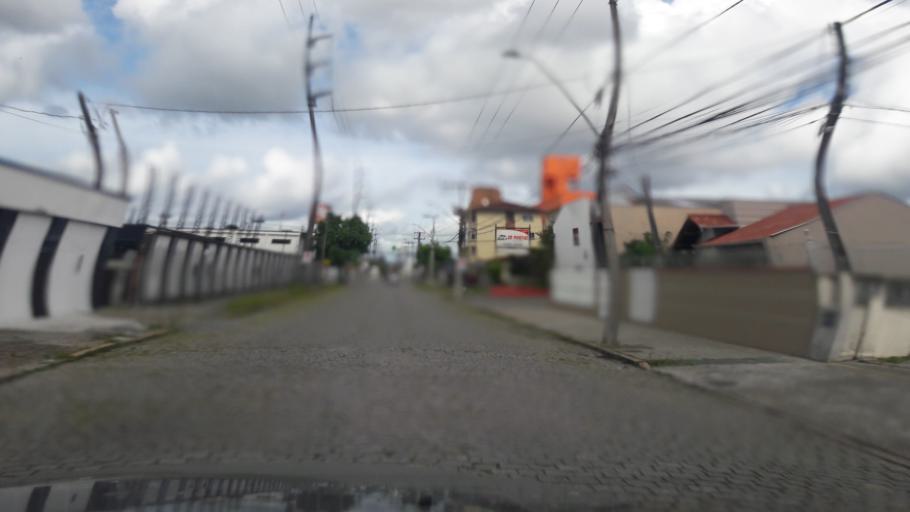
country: BR
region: Santa Catarina
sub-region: Joinville
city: Joinville
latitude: -26.3190
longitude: -48.8439
